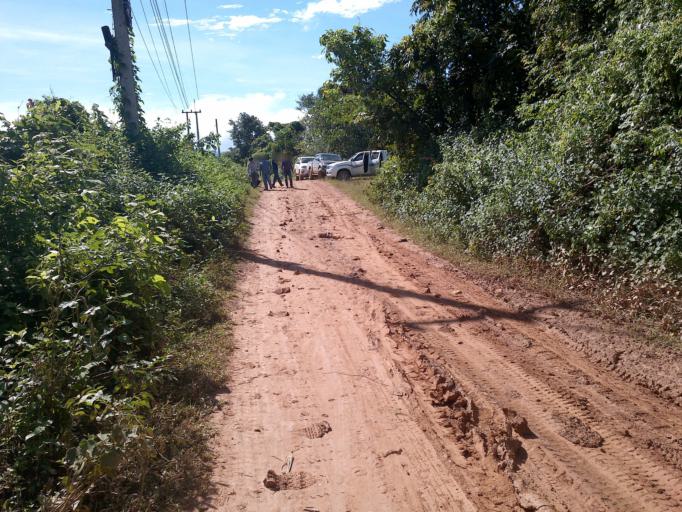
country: TH
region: Nan
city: Chaloem Phra Kiat
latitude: 19.9651
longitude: 101.1388
